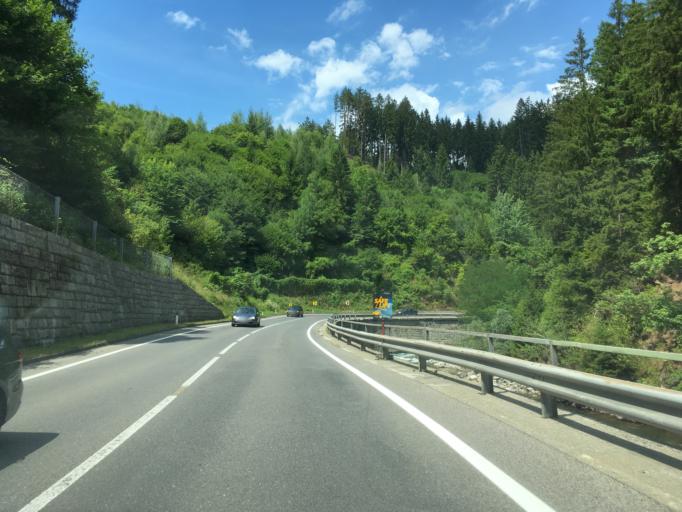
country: AT
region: Carinthia
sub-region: Politischer Bezirk Spittal an der Drau
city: Spittal an der Drau
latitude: 46.8127
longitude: 13.4910
